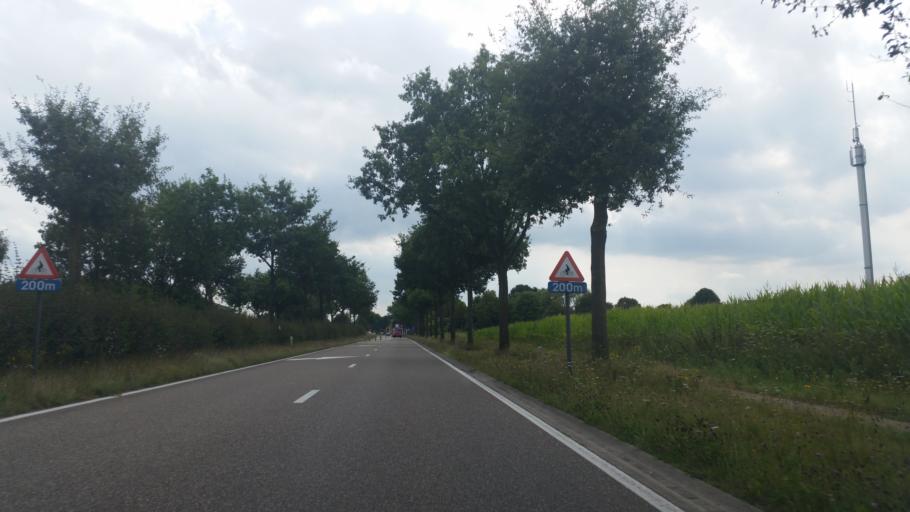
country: BE
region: Flanders
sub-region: Provincie Antwerpen
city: Turnhout
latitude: 51.2844
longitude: 4.9541
